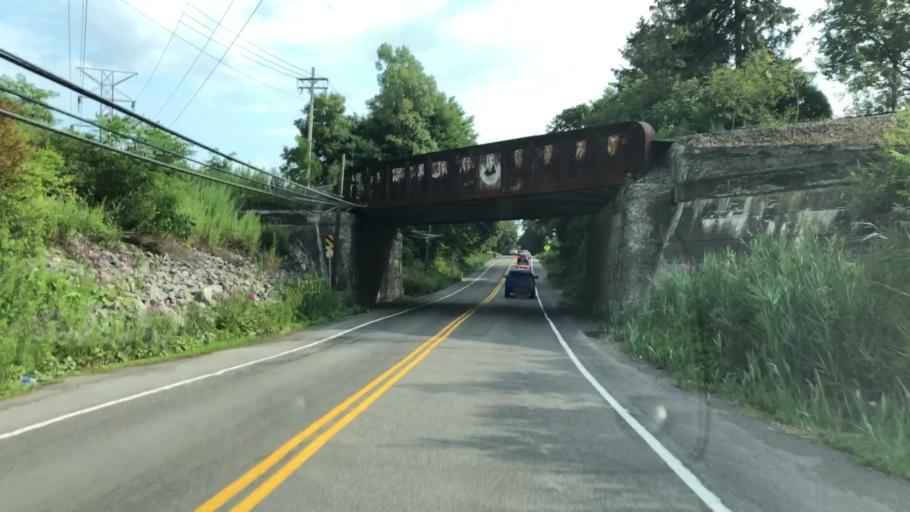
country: US
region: New York
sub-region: Erie County
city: Elma Center
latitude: 42.8289
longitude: -78.6365
